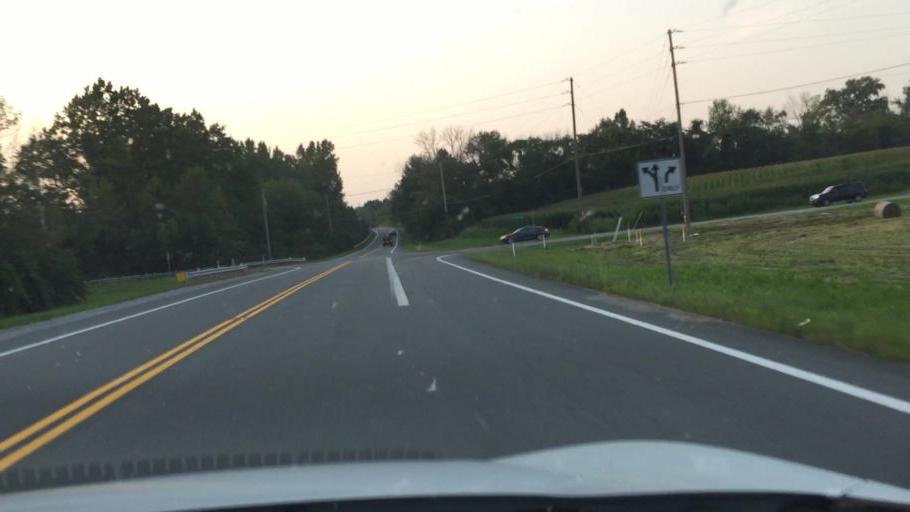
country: US
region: Ohio
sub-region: Madison County
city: Choctaw Lake
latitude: 39.9473
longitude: -83.5029
